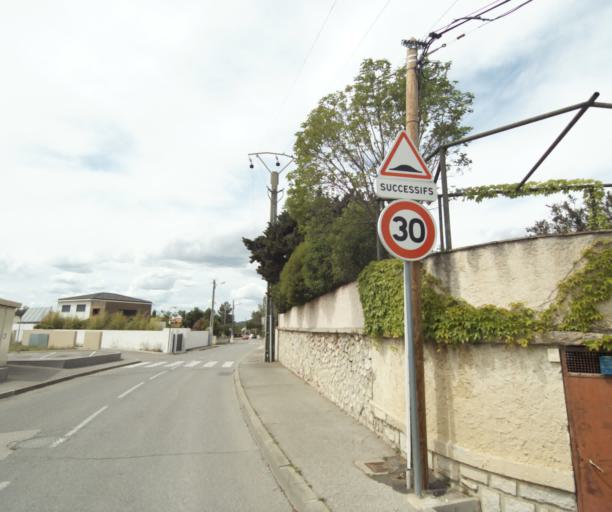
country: FR
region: Provence-Alpes-Cote d'Azur
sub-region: Departement des Bouches-du-Rhone
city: Rognac
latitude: 43.4820
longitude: 5.2377
